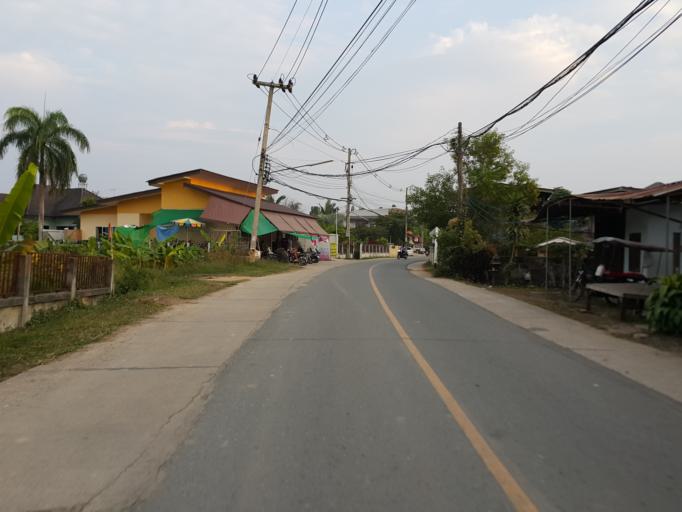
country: TH
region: Chiang Mai
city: San Sai
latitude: 18.8851
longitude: 99.1246
